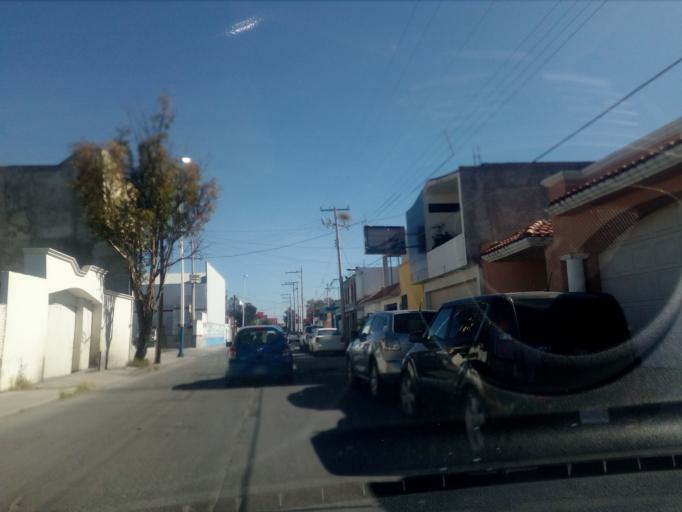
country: MX
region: Durango
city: Victoria de Durango
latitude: 24.0048
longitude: -104.6580
